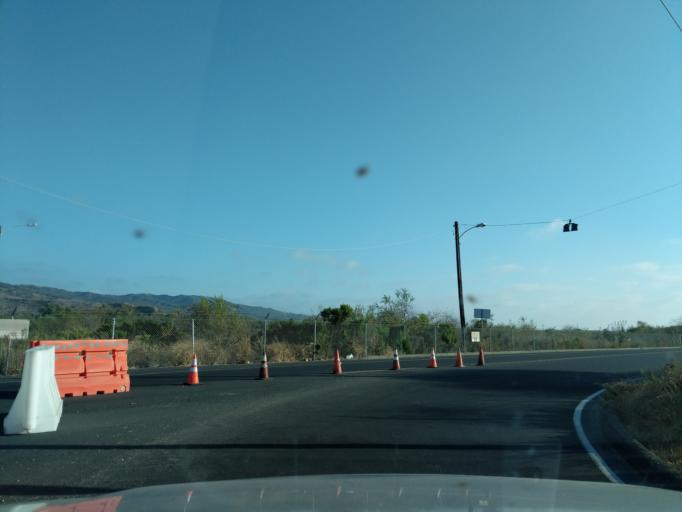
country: US
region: California
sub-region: Orange County
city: San Clemente
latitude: 33.4261
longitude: -117.5708
